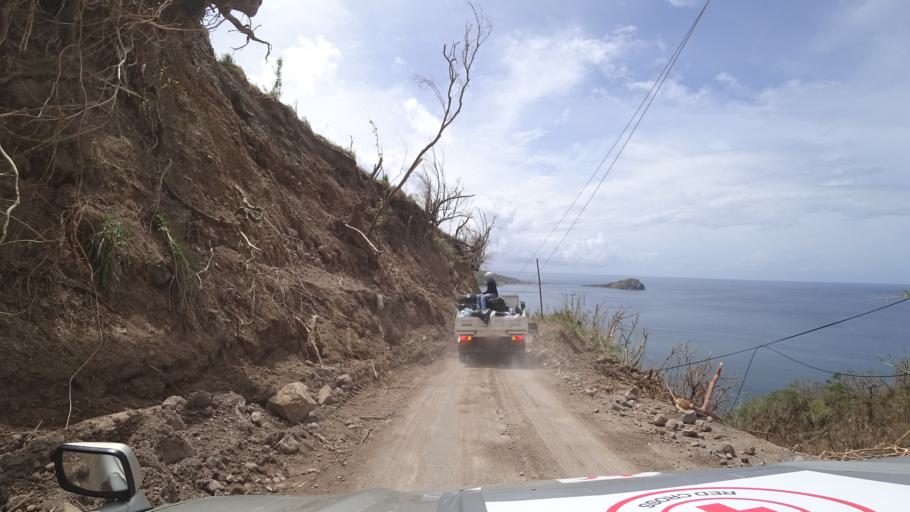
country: DM
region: Saint Mark
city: Soufriere
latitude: 15.2360
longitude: -61.3642
